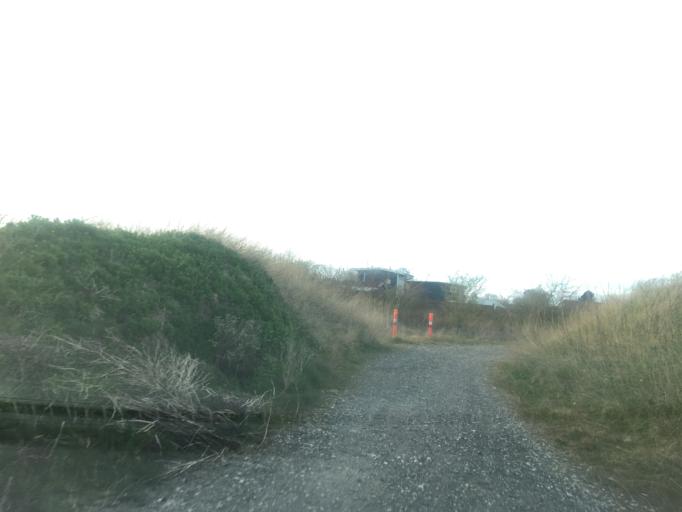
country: DK
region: Capital Region
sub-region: Tarnby Kommune
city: Tarnby
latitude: 55.5899
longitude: 12.5875
